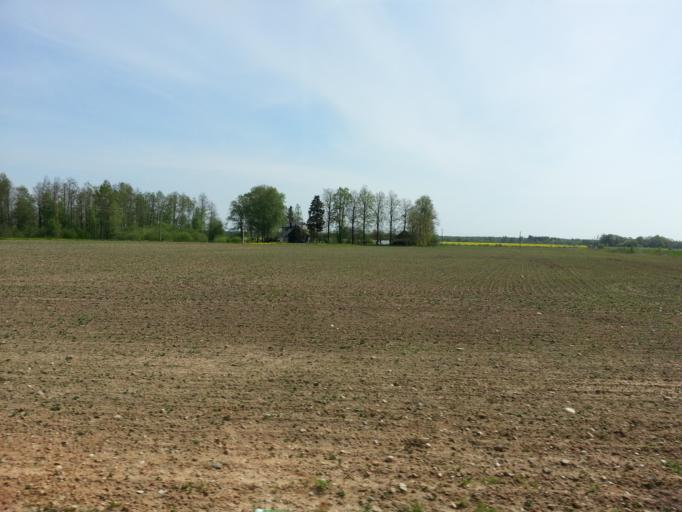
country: LT
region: Panevezys
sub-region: Panevezys City
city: Panevezys
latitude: 55.8519
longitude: 24.2449
